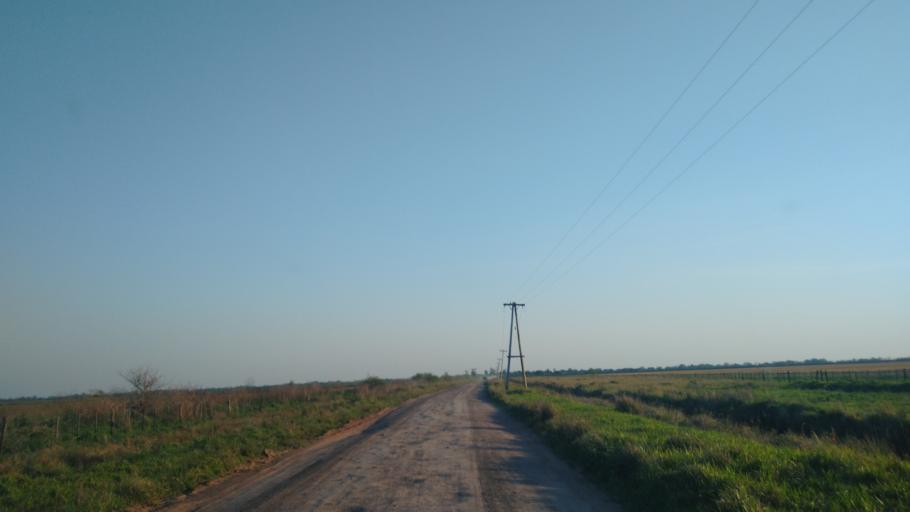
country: PY
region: Neembucu
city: Cerrito
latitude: -27.3896
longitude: -57.6583
